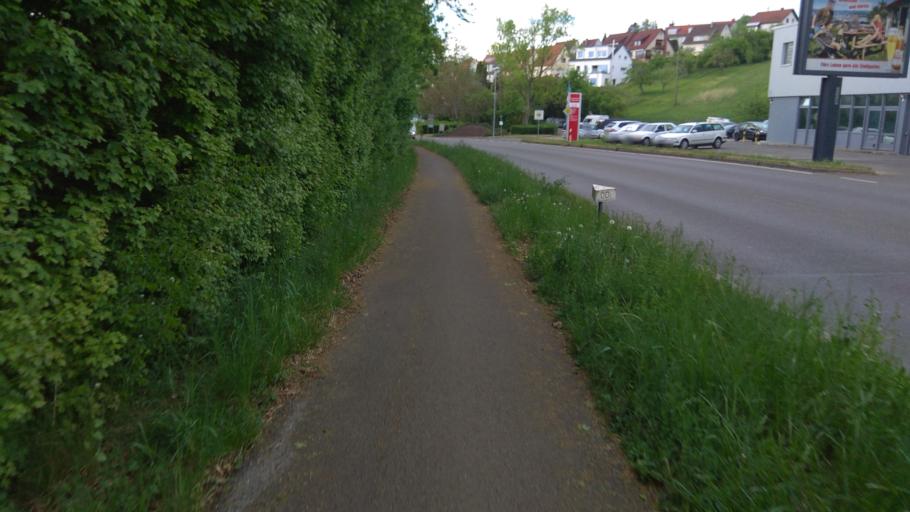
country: DE
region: Baden-Wuerttemberg
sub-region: Tuebingen Region
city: Wannweil
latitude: 48.5076
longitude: 9.1631
